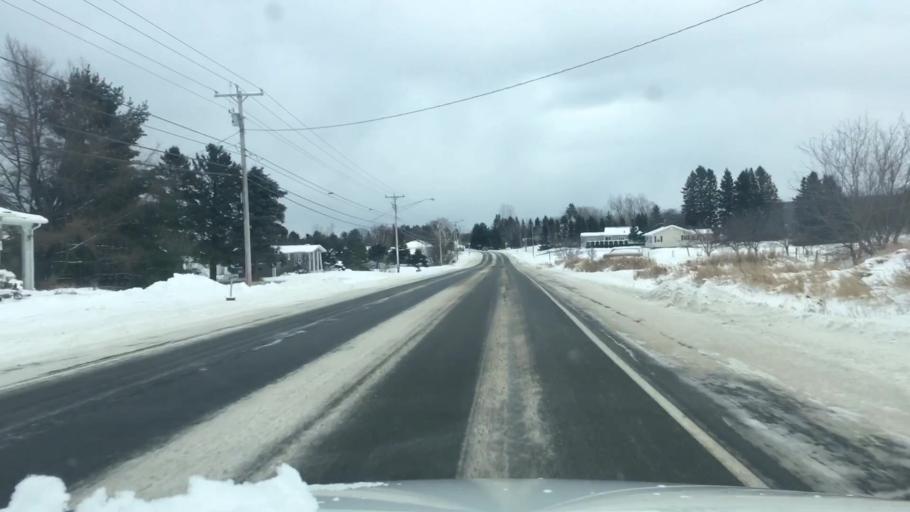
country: US
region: Maine
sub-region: Aroostook County
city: Madawaska
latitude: 47.3472
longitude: -68.2684
